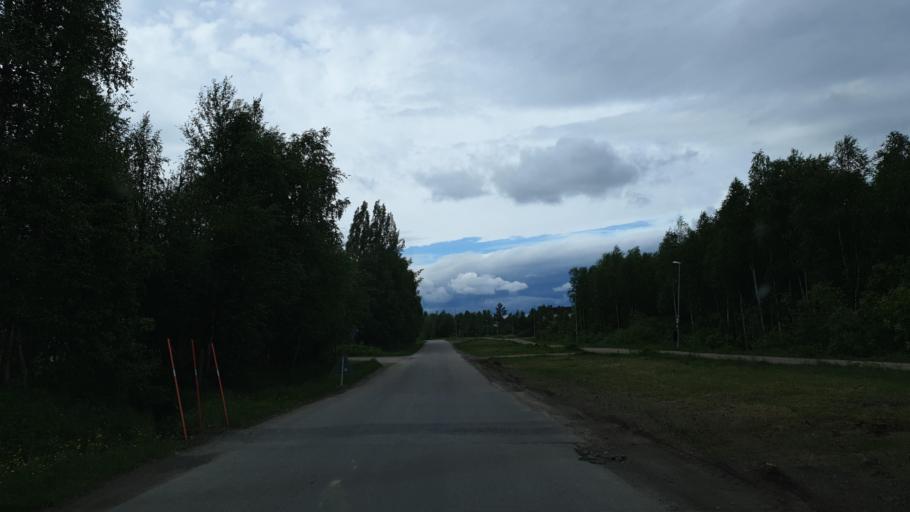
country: SE
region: Norrbotten
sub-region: Gallivare Kommun
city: Gaellivare
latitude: 67.1291
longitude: 20.6485
